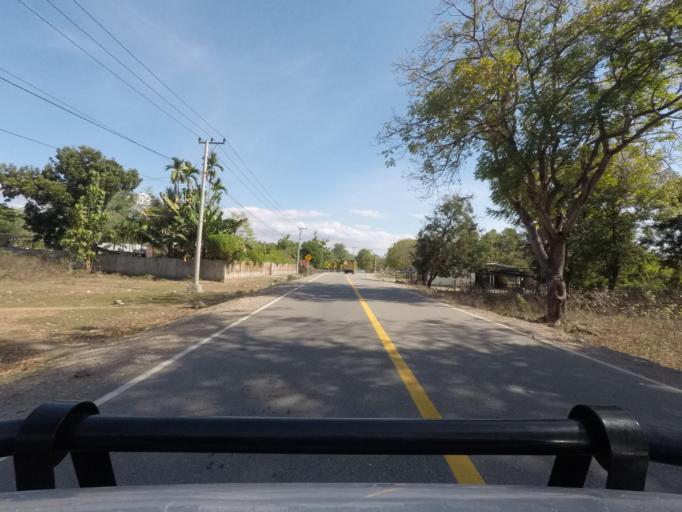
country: ID
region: East Nusa Tenggara
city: Atambua
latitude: -8.9223
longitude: 124.9917
